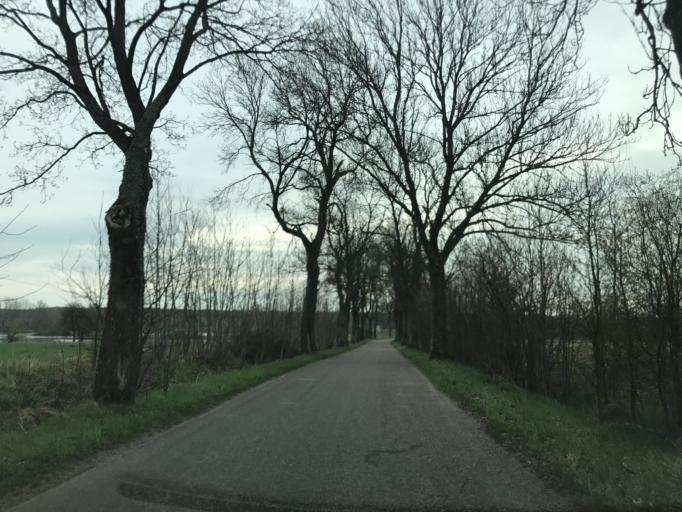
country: PL
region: Warmian-Masurian Voivodeship
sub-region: Powiat olsztynski
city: Olsztynek
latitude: 53.6288
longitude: 20.2090
